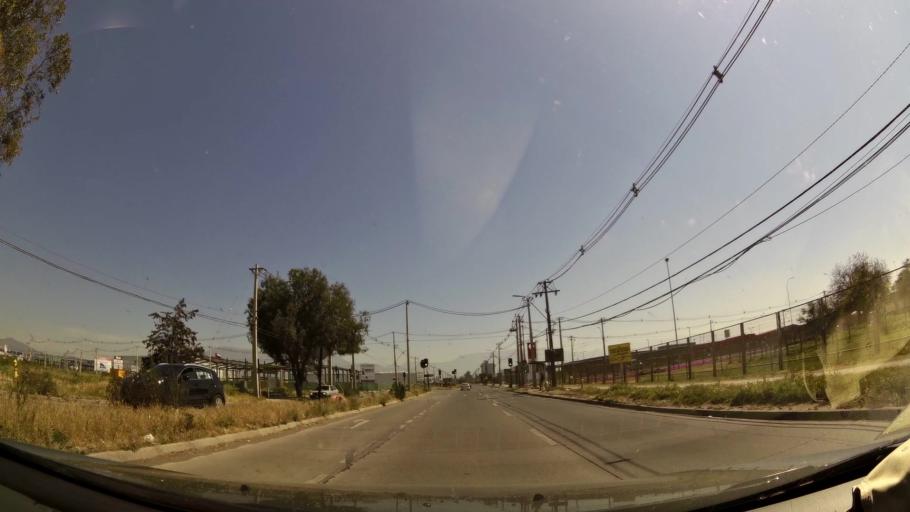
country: CL
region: Santiago Metropolitan
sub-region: Provincia de Santiago
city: Lo Prado
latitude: -33.3976
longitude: -70.7606
